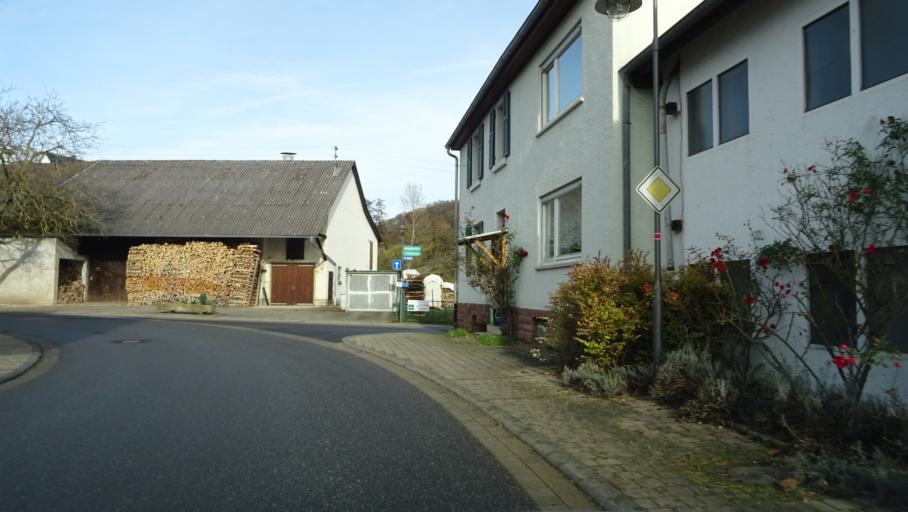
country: DE
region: Baden-Wuerttemberg
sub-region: Karlsruhe Region
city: Mosbach
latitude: 49.3730
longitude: 9.1259
